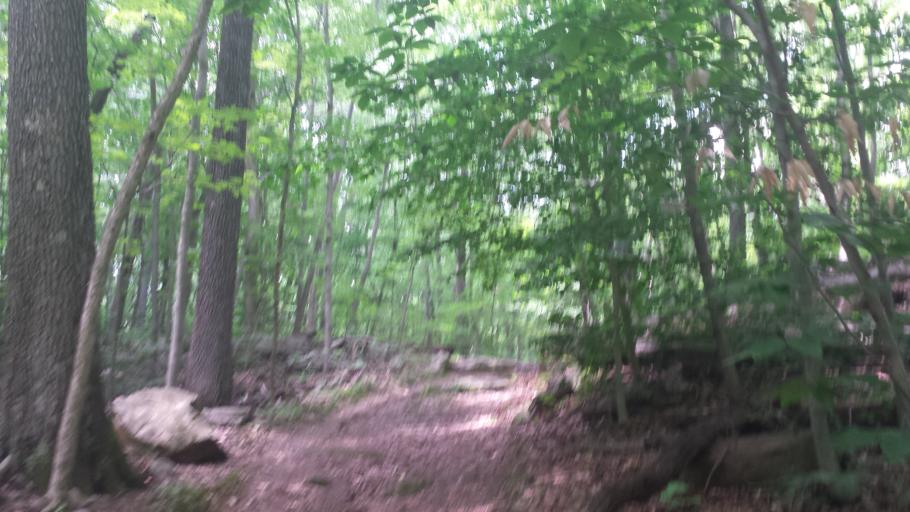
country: US
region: New York
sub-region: Westchester County
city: Scarsdale
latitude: 40.9878
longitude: -73.7506
